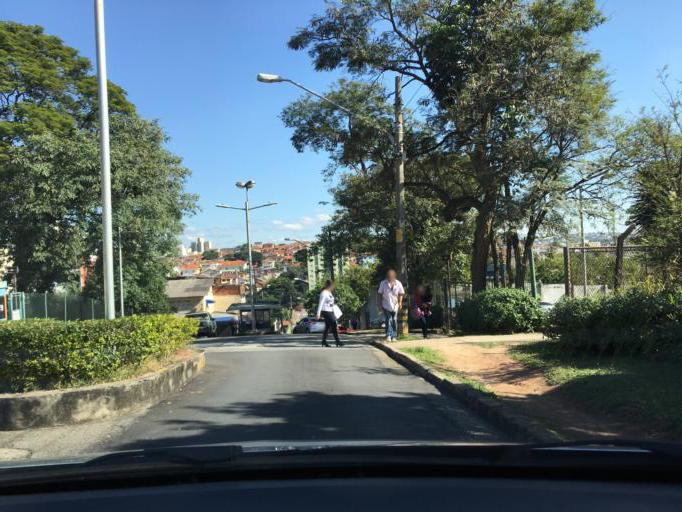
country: BR
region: Sao Paulo
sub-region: Osasco
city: Osasco
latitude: -23.5639
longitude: -46.7422
